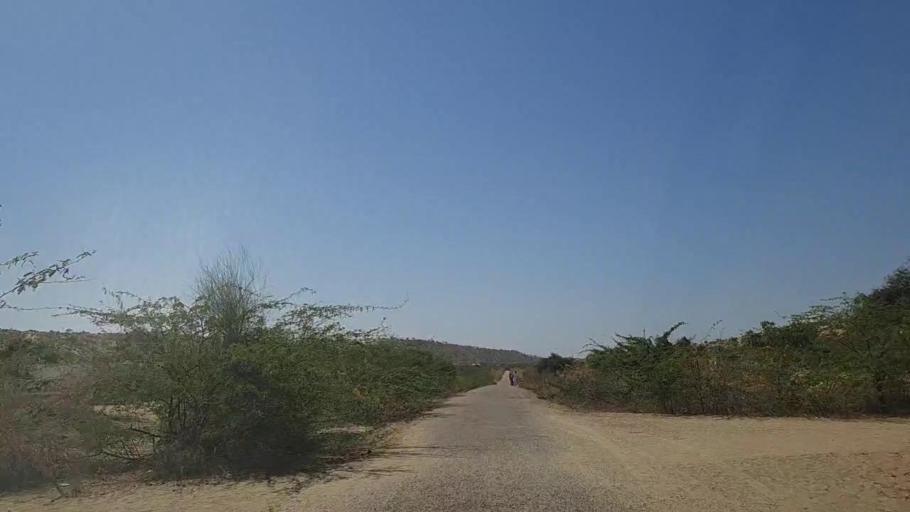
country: PK
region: Sindh
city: Mithi
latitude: 24.7992
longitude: 69.7154
